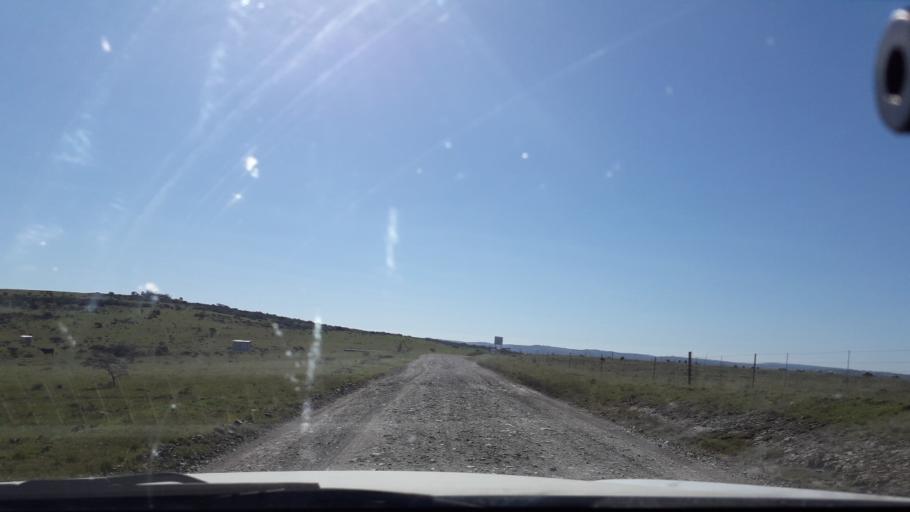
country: ZA
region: Eastern Cape
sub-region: Amathole District Municipality
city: Komga
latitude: -32.7934
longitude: 27.9515
